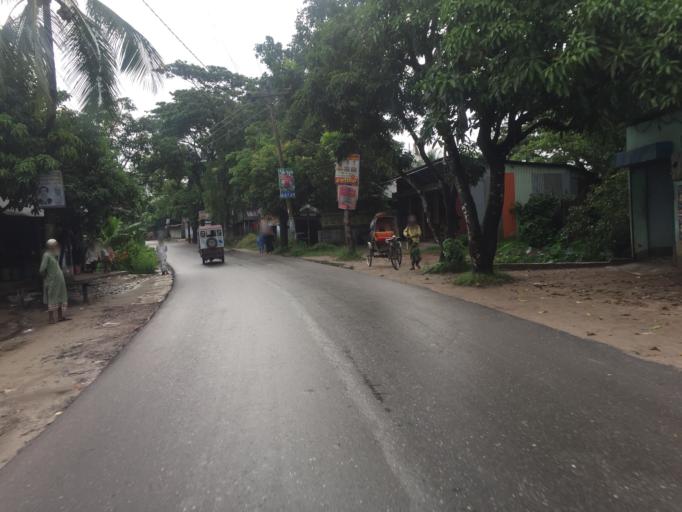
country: BD
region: Dhaka
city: Narayanganj
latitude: 23.5517
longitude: 90.5013
